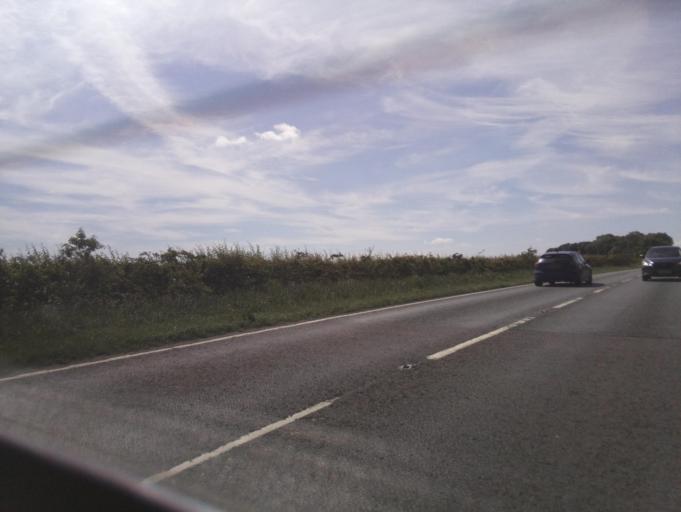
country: GB
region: England
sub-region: Lincolnshire
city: Burton
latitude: 53.3658
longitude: -0.5453
